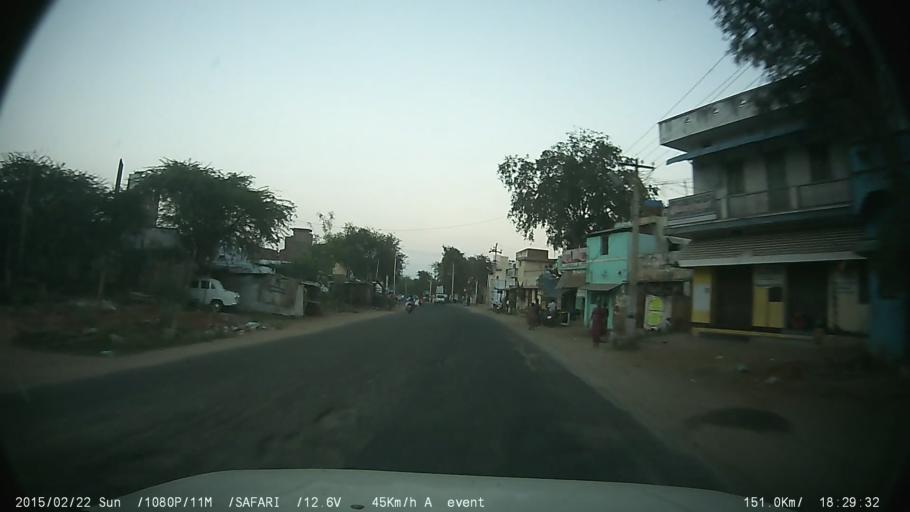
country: IN
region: Tamil Nadu
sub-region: Theni
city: Teni
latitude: 9.9848
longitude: 77.4548
